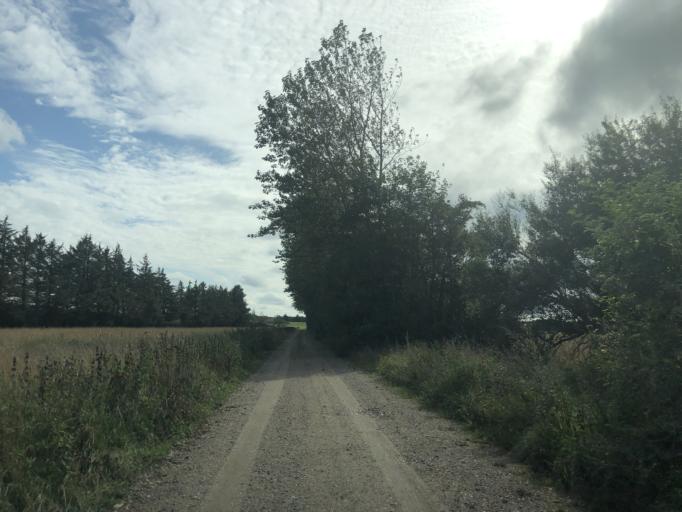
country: DK
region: Central Jutland
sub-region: Holstebro Kommune
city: Ulfborg
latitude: 56.2434
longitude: 8.4480
